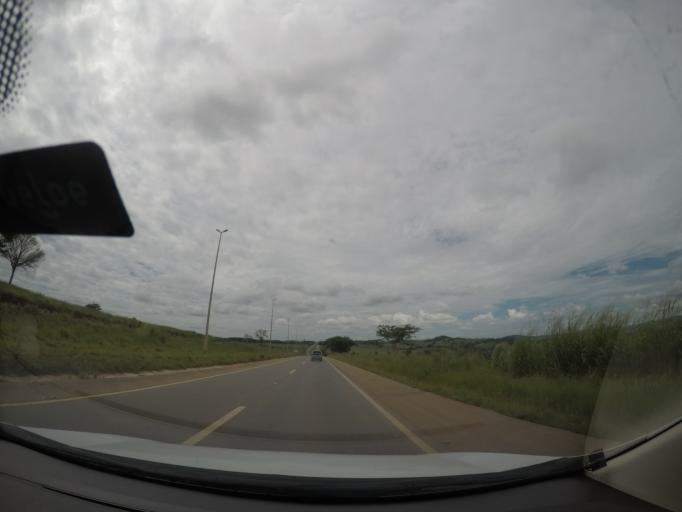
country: BR
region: Goias
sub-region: Inhumas
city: Inhumas
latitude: -16.4107
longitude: -49.4756
